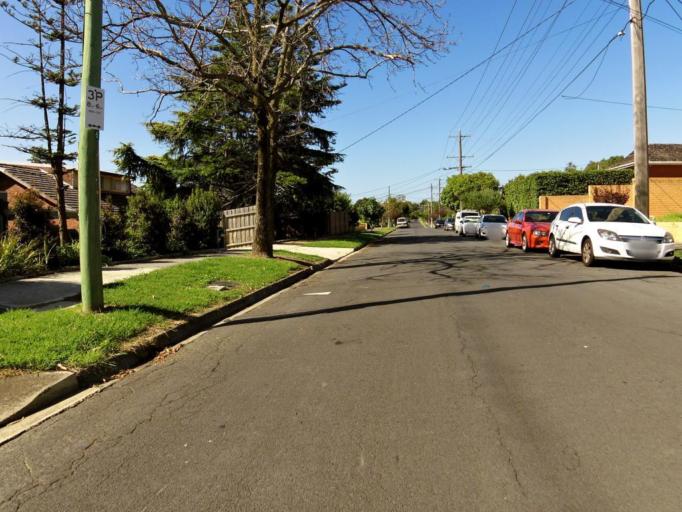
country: AU
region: Victoria
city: Ashburton
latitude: -37.8748
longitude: 145.0862
